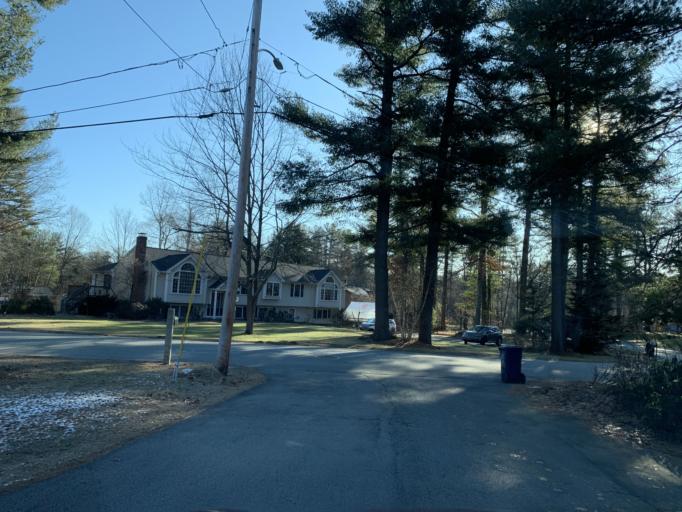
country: US
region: Massachusetts
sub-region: Middlesex County
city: Dracut
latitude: 42.7116
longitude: -71.2709
